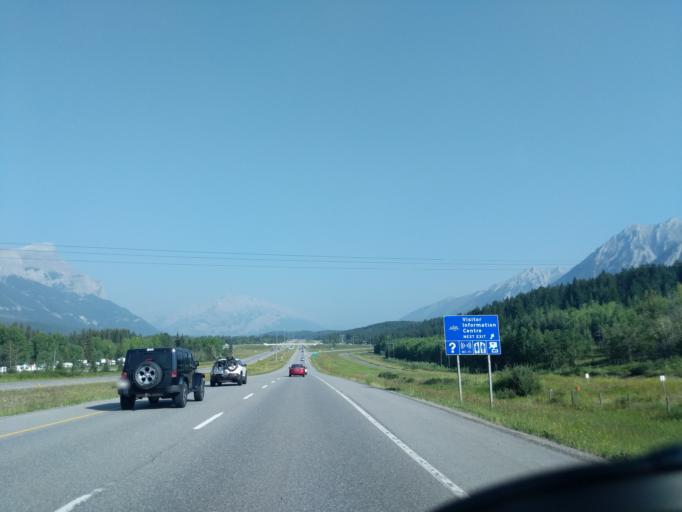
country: CA
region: Alberta
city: Canmore
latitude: 51.1040
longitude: -115.3610
